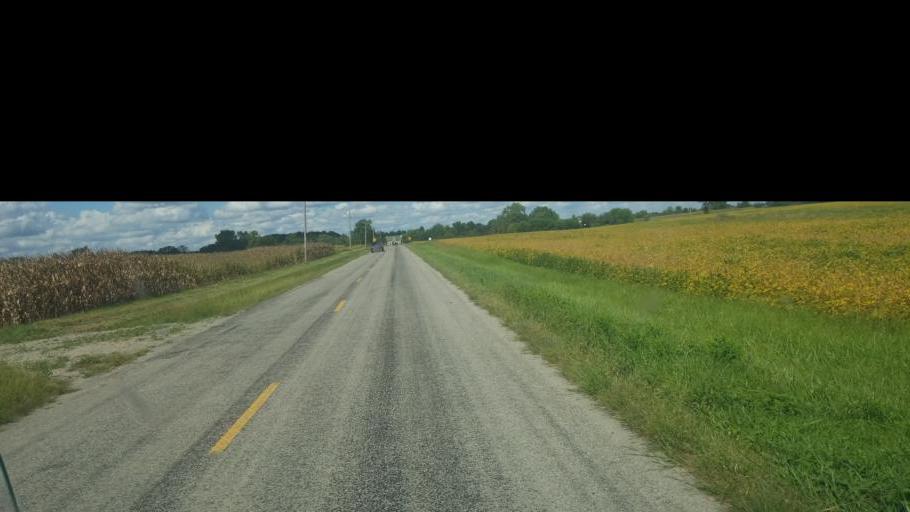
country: US
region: Ohio
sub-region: Champaign County
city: North Lewisburg
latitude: 40.4069
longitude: -83.5002
